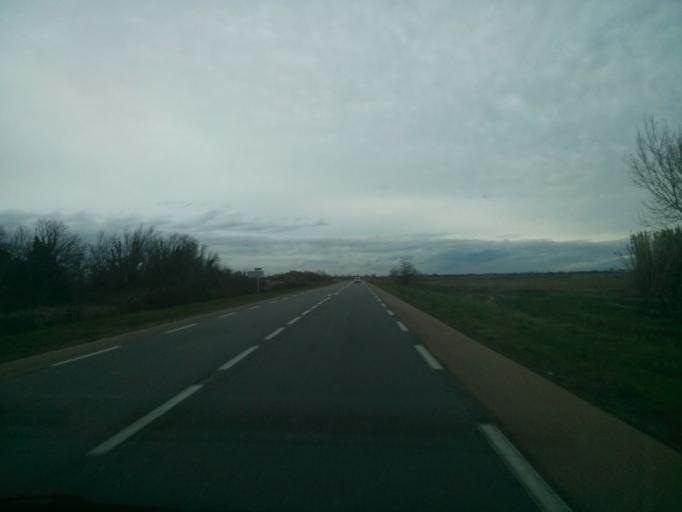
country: FR
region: Languedoc-Roussillon
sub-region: Departement du Gard
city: Fourques
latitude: 43.6829
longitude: 4.5421
